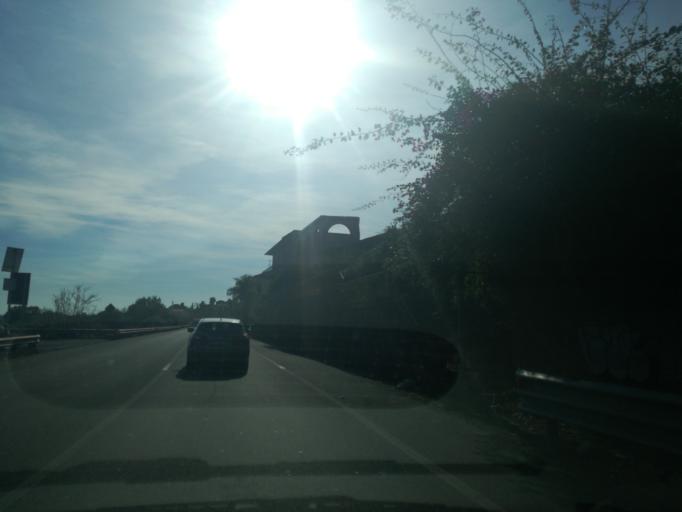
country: IT
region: Sicily
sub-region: Catania
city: Acireale
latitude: 37.6103
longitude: 15.1697
